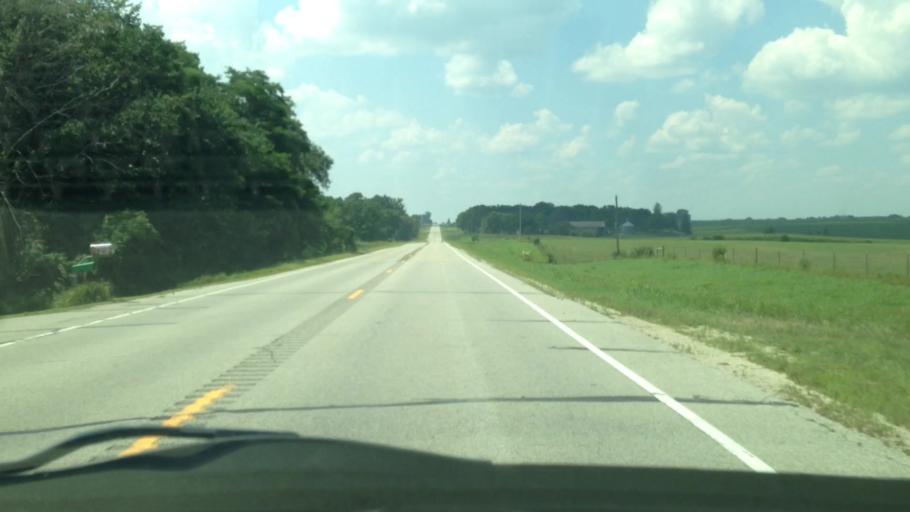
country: US
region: Minnesota
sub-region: Olmsted County
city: Stewartville
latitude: 43.8554
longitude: -92.4082
